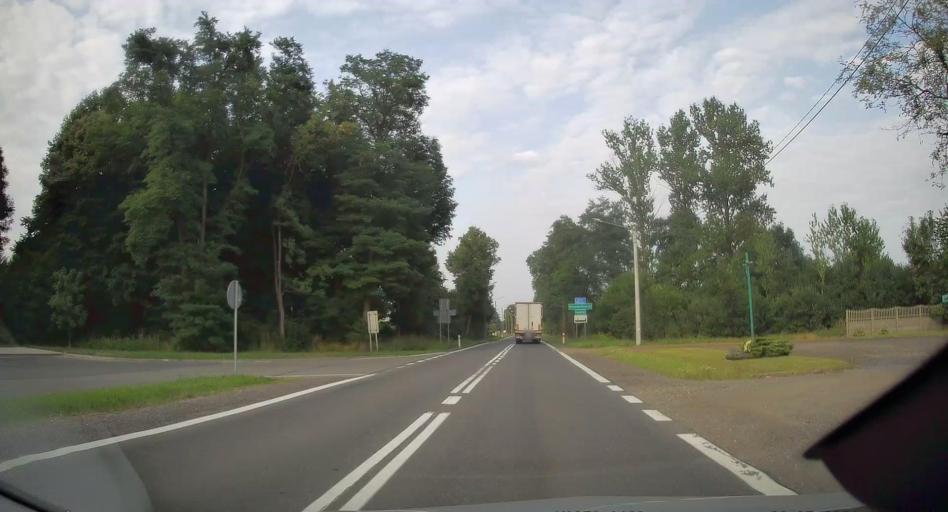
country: PL
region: Silesian Voivodeship
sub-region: Powiat czestochowski
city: Rudniki
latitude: 50.8889
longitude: 19.2652
